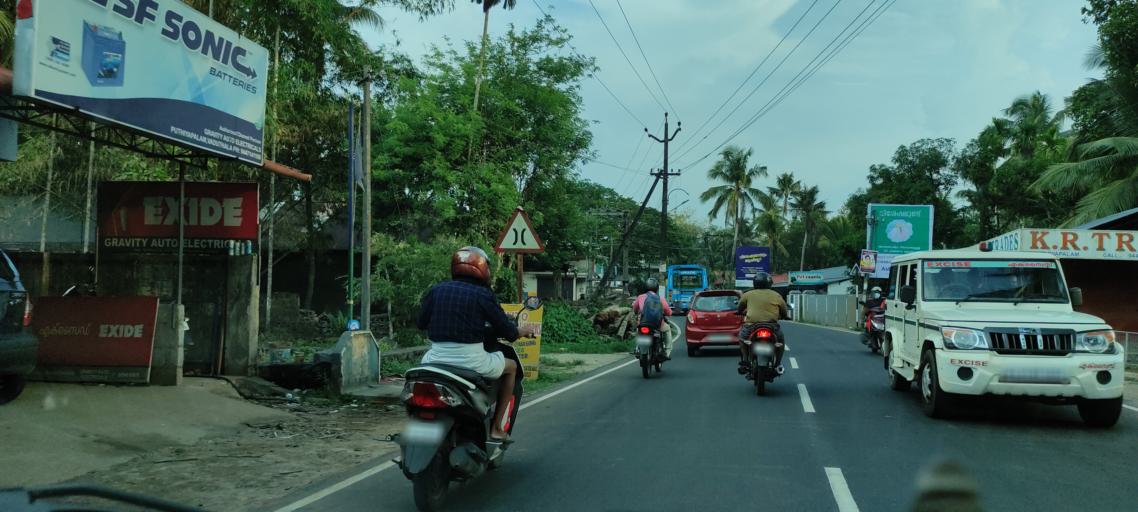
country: IN
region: Kerala
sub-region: Alappuzha
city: Arukutti
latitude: 9.8485
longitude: 76.3286
